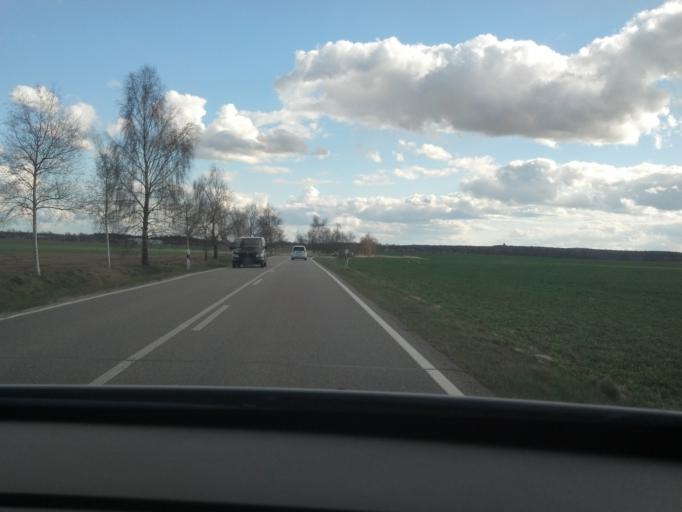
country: DE
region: Mecklenburg-Vorpommern
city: Burg Stargard
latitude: 53.5175
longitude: 13.3174
